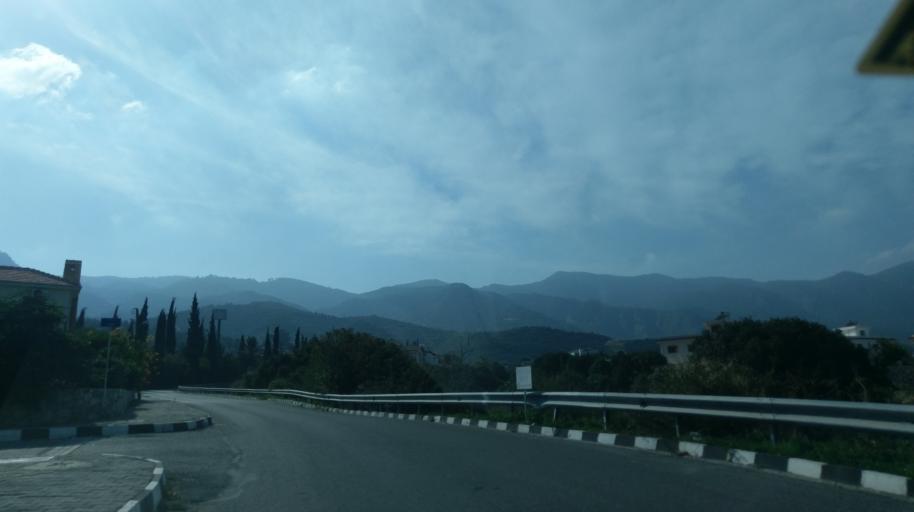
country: CY
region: Keryneia
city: Lapithos
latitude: 35.3409
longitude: 33.2181
